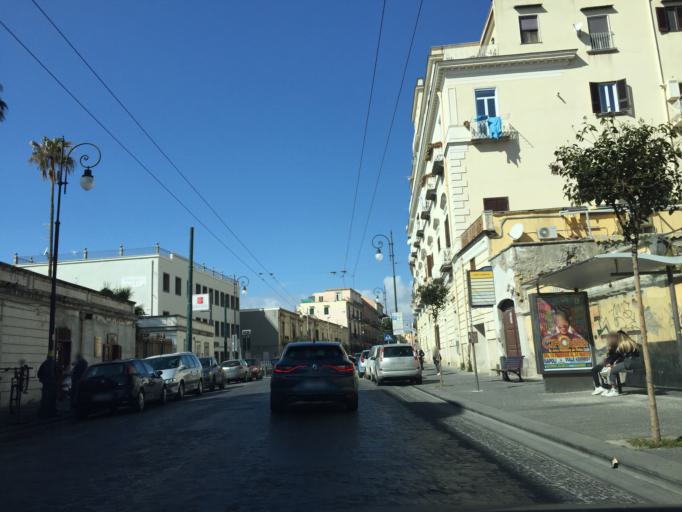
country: IT
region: Campania
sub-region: Provincia di Napoli
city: Portici
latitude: 40.8187
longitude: 14.3296
